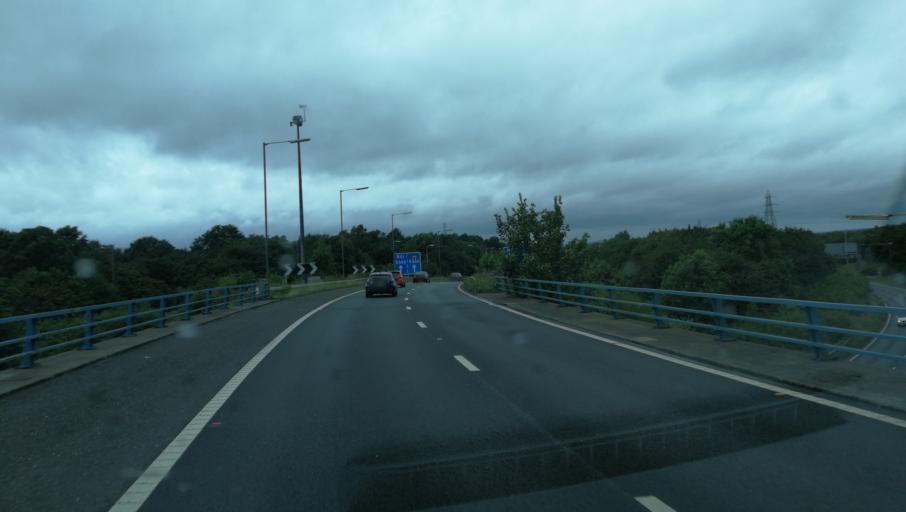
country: GB
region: England
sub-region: Borough of Bolton
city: Kearsley
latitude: 53.5243
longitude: -2.3609
